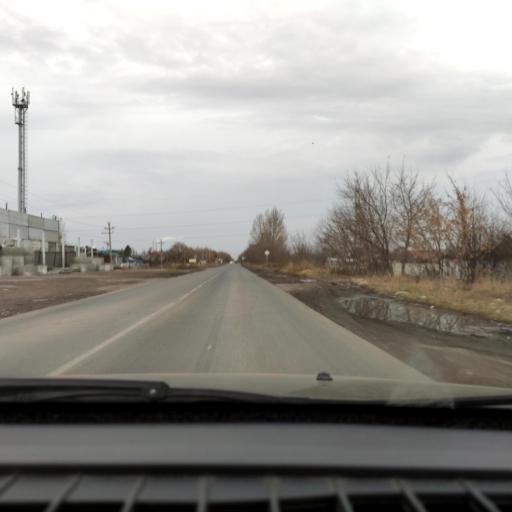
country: RU
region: Samara
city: Tol'yatti
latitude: 53.5750
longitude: 49.3329
